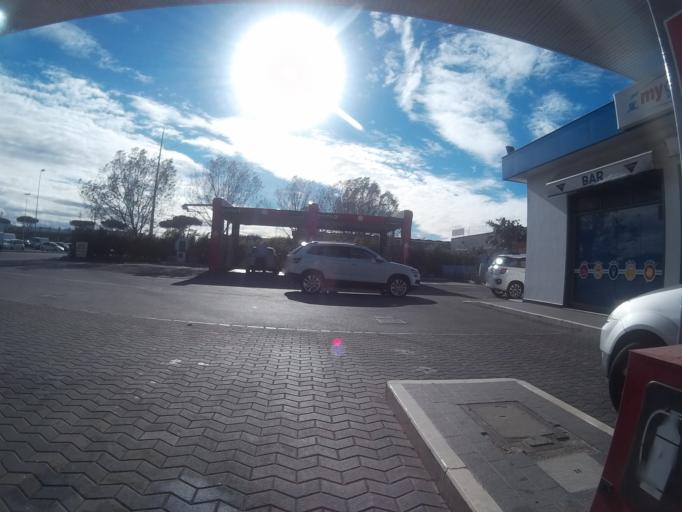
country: IT
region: Tuscany
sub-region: Provincia di Livorno
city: Livorno
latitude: 43.5652
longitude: 10.3417
